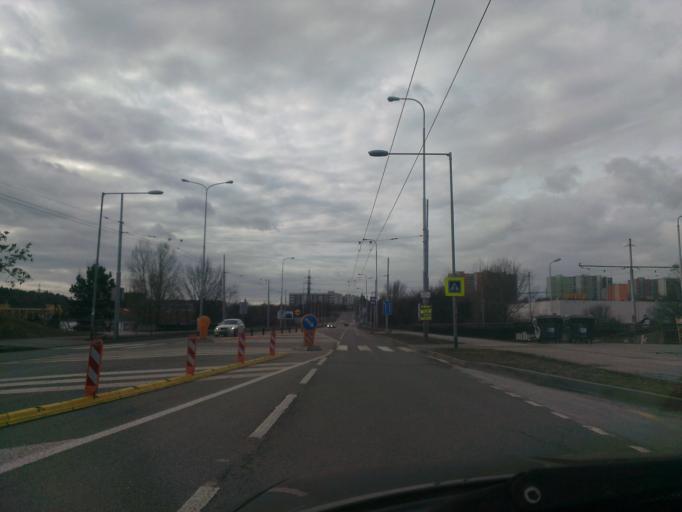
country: CZ
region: South Moravian
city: Bilovice nad Svitavou
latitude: 49.2018
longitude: 16.6703
